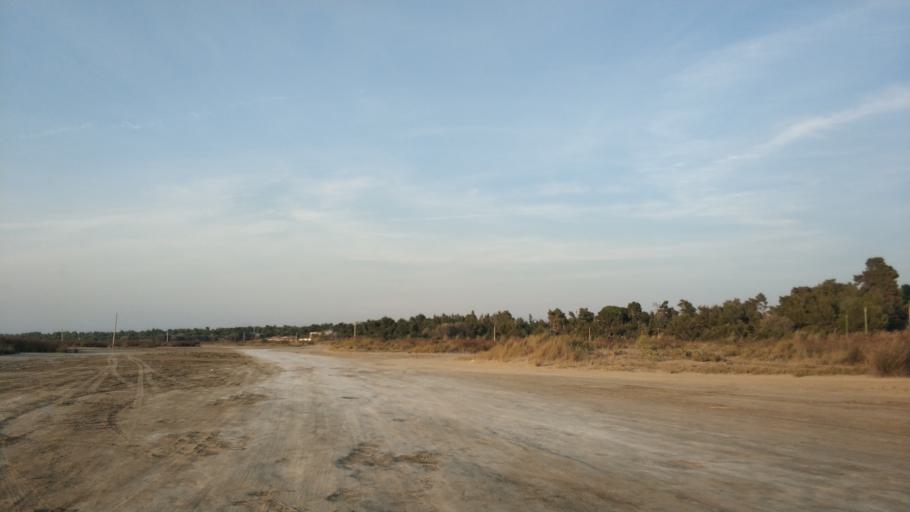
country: AL
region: Fier
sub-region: Rrethi i Lushnjes
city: Divjake
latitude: 40.9645
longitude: 19.4744
